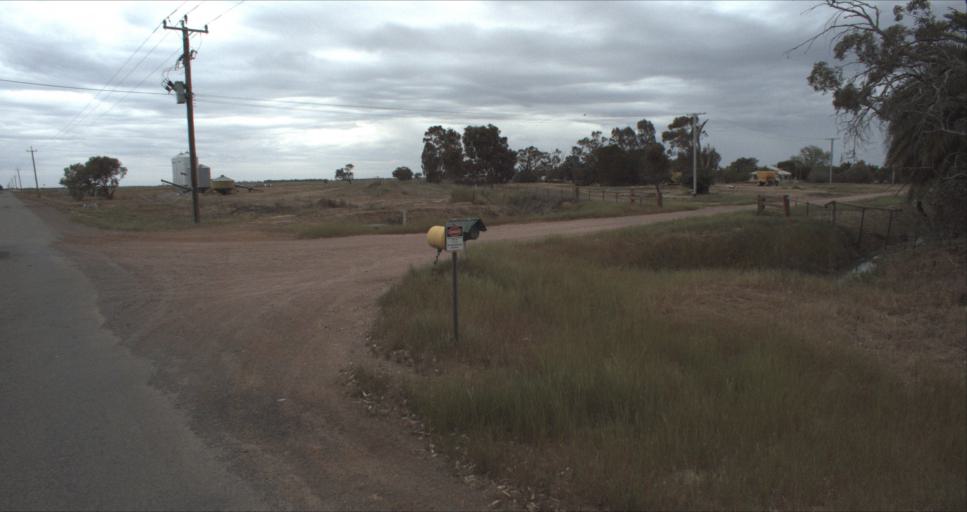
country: AU
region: New South Wales
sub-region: Leeton
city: Leeton
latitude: -34.4205
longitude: 146.3386
